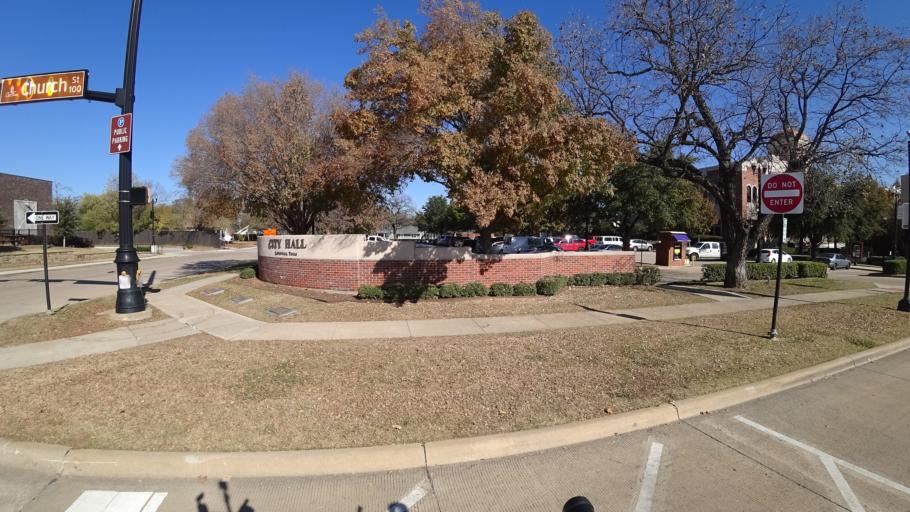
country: US
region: Texas
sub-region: Denton County
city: Lewisville
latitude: 33.0473
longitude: -96.9963
